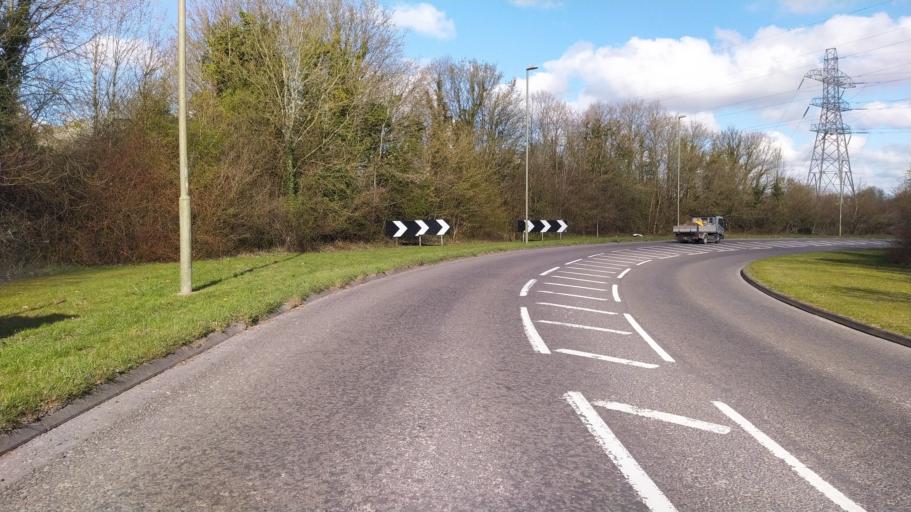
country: GB
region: England
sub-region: Hampshire
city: Andover
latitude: 51.2163
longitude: -1.4927
